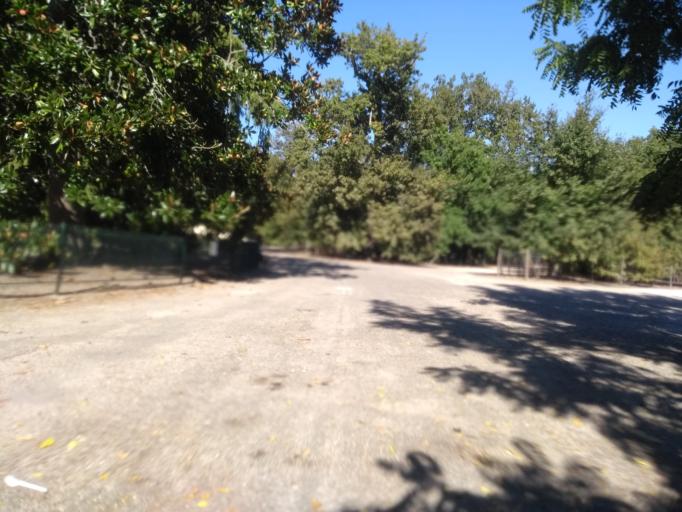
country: FR
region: Aquitaine
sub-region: Departement de la Gironde
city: Le Bouscat
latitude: 44.8525
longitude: -0.6016
